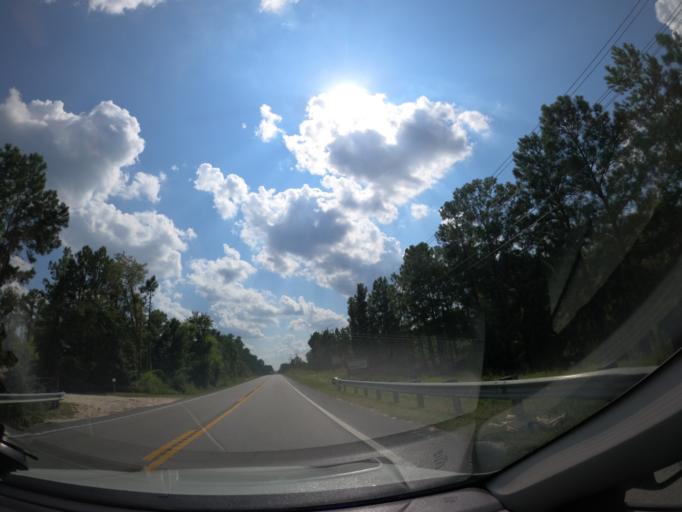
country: US
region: South Carolina
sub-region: Lexington County
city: South Congaree
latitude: 33.8804
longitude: -81.1748
